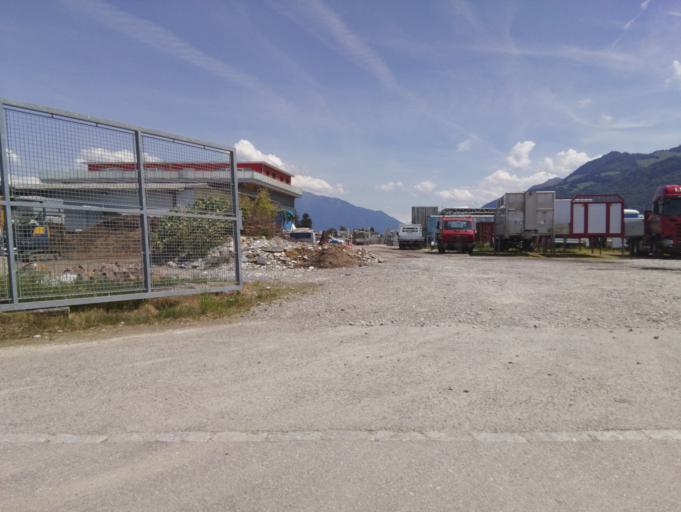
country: CH
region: Schwyz
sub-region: Bezirk March
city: Lachen
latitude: 47.1862
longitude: 8.8922
